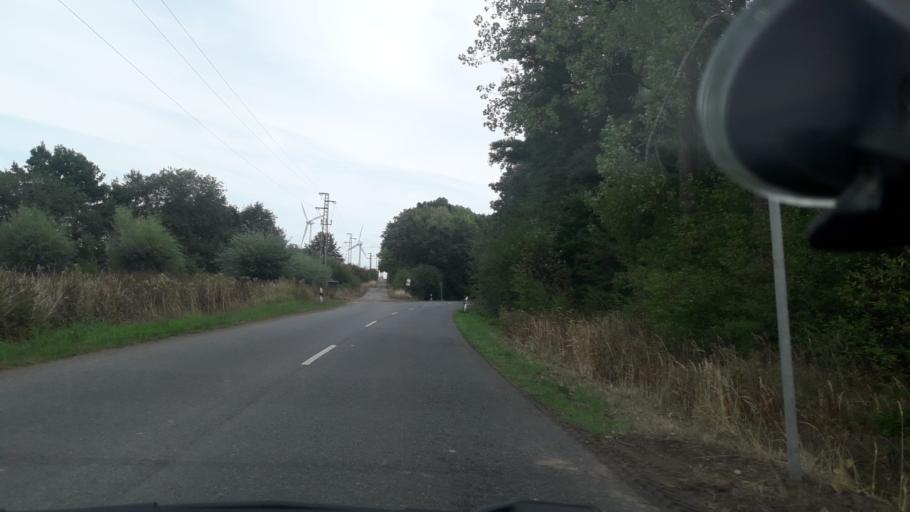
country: DE
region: Lower Saxony
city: Gross Twulpstedt
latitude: 52.3502
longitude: 10.8623
